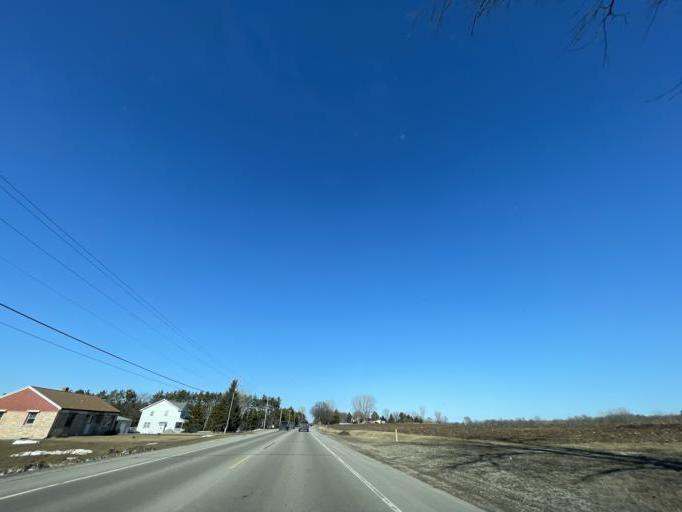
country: US
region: Wisconsin
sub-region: Brown County
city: Suamico
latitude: 44.6077
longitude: -88.0744
